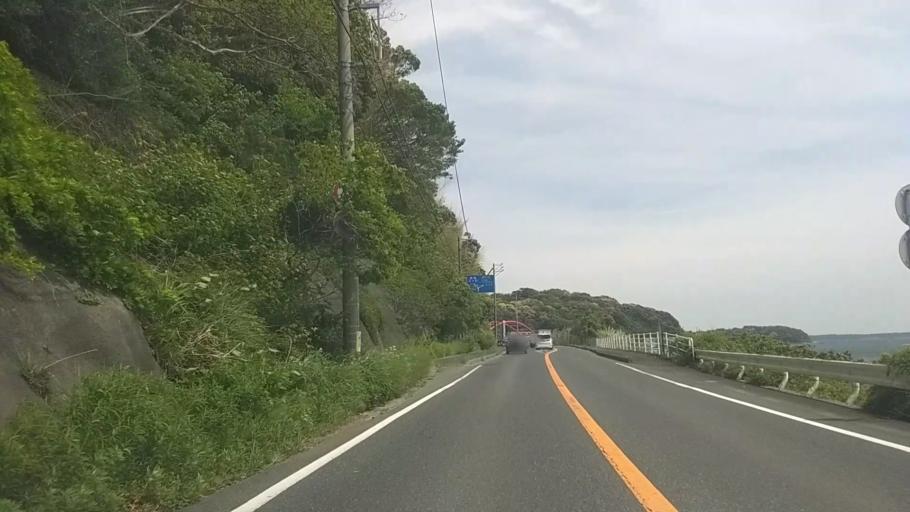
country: JP
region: Shizuoka
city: Kosai-shi
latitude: 34.7702
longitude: 137.5440
